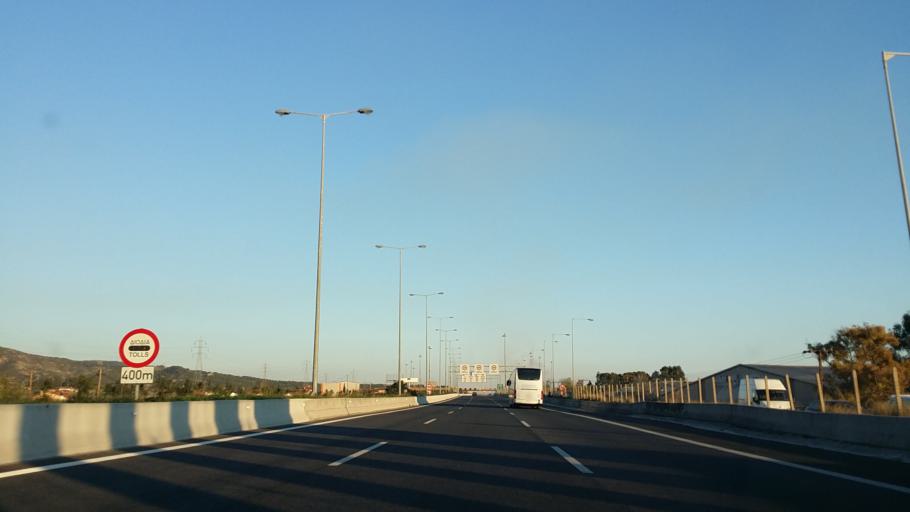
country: GR
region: Peloponnese
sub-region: Nomos Korinthias
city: Isthmia
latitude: 37.9258
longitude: 23.0214
